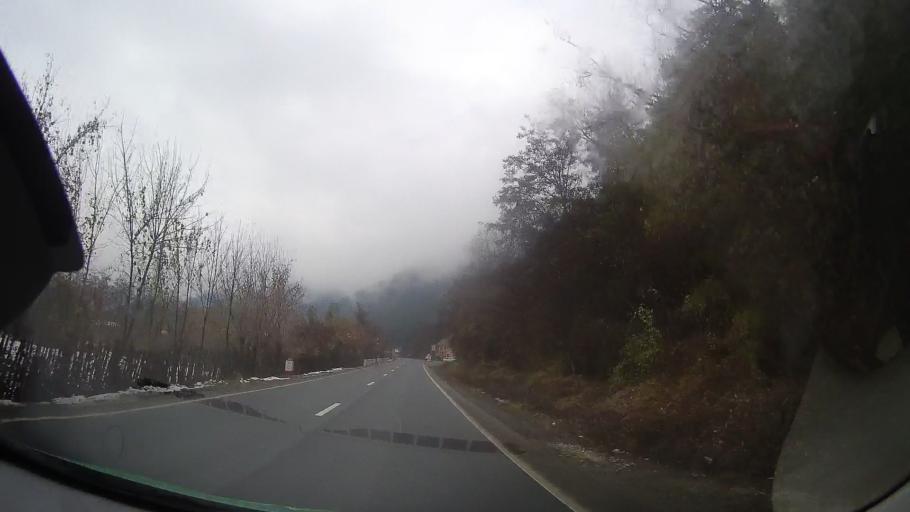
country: RO
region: Neamt
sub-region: Comuna Bicaz Chei
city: Bicaz Chei
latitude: 46.8414
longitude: 25.9017
